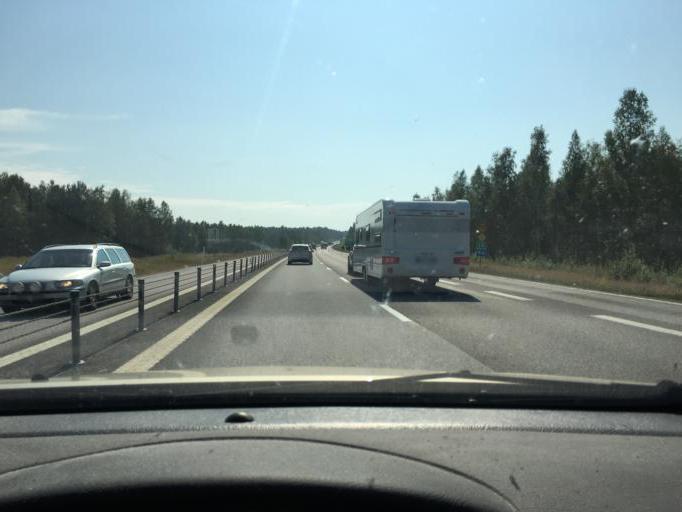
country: SE
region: Norrbotten
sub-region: Lulea Kommun
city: Gammelstad
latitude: 65.6126
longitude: 22.0557
